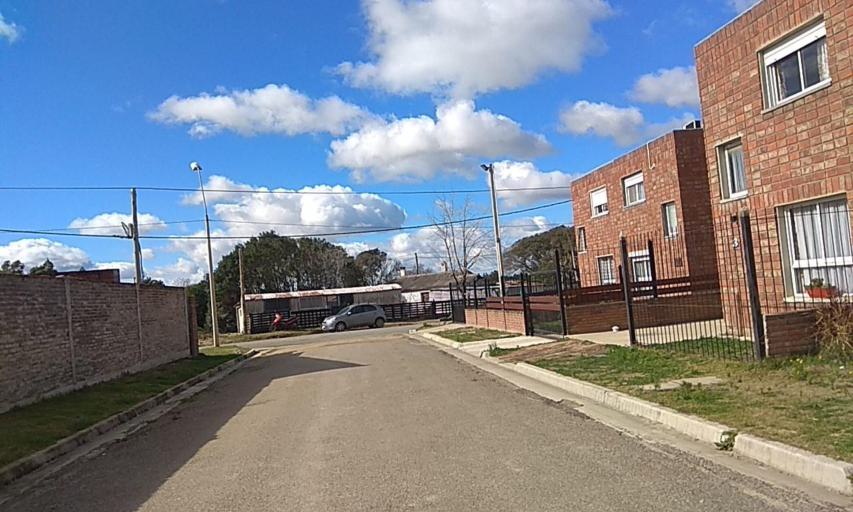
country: UY
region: Florida
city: Florida
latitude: -34.0968
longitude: -56.2336
